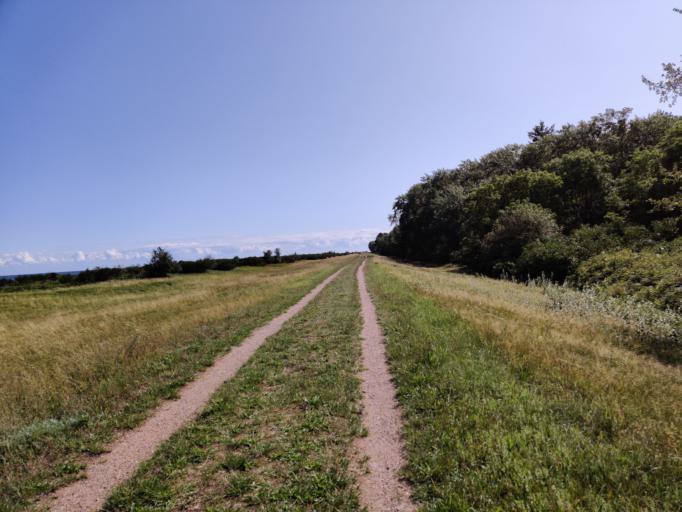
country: DK
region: Zealand
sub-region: Guldborgsund Kommune
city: Nykobing Falster
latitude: 54.6125
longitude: 11.9650
